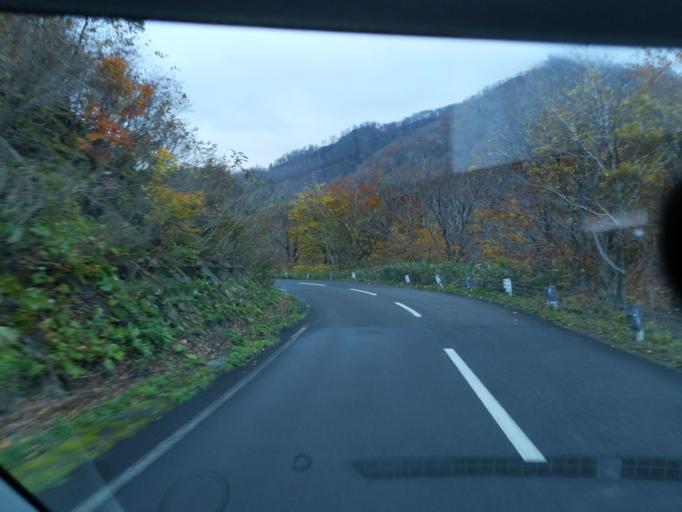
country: JP
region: Iwate
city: Mizusawa
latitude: 39.1176
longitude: 140.8338
